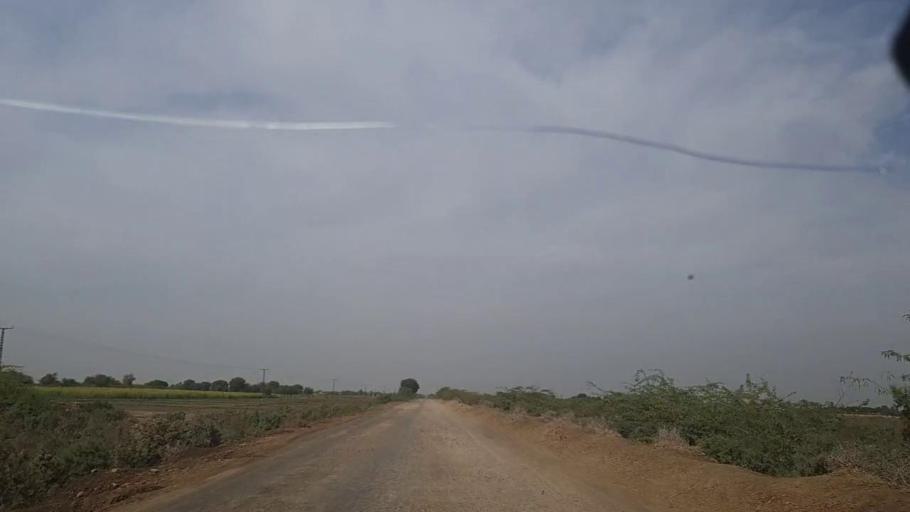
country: PK
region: Sindh
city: Pithoro
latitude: 25.5555
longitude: 69.3628
